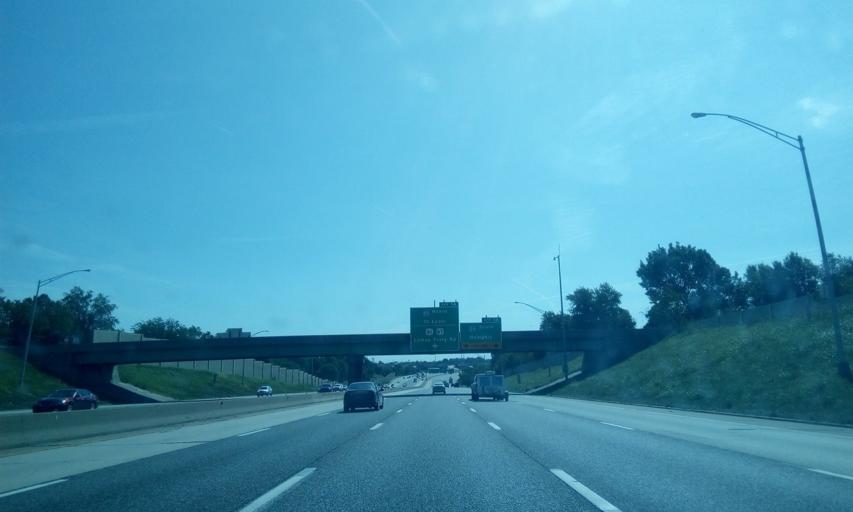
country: US
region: Missouri
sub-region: Saint Louis County
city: Concord
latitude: 38.5085
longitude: -90.3549
